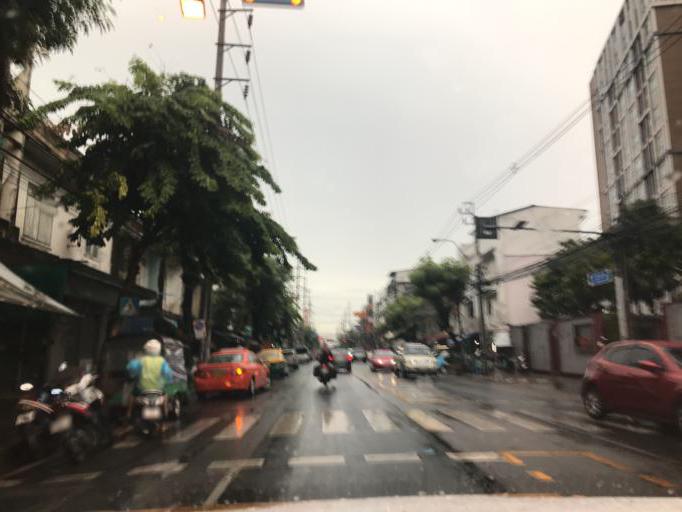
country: TH
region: Bangkok
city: Bangkok Noi
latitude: 13.7572
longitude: 100.4779
